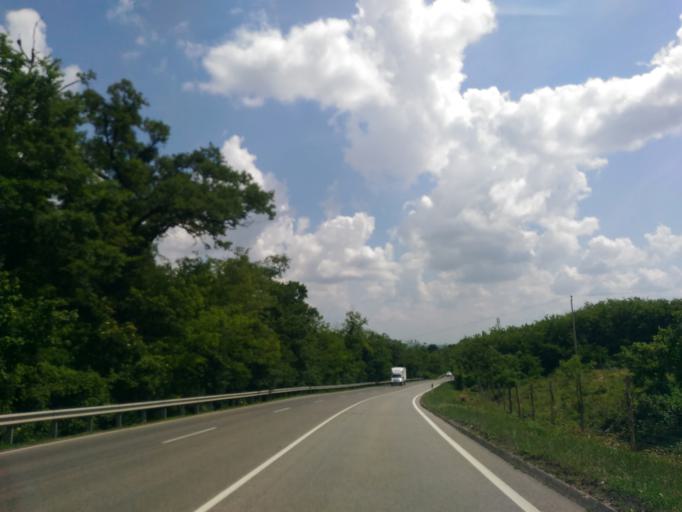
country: HU
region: Baranya
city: Pecs
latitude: 46.1257
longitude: 18.2587
